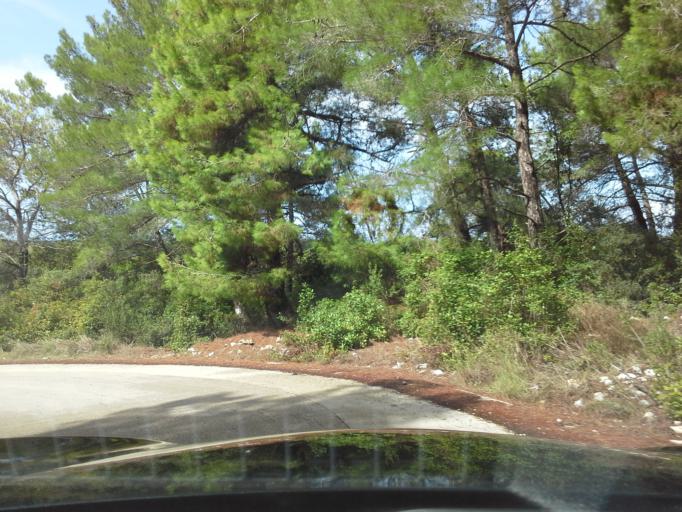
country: HR
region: Primorsko-Goranska
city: Mali Losinj
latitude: 44.5759
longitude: 14.4161
